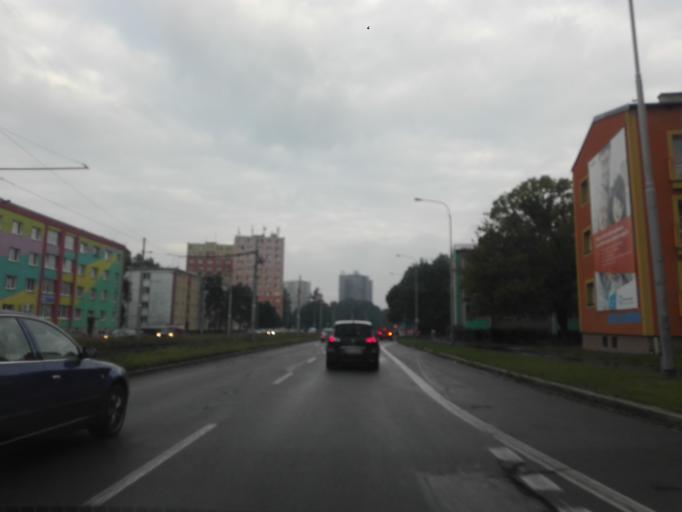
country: CZ
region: Moravskoslezsky
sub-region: Okres Ostrava-Mesto
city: Ostrava
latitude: 49.7915
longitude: 18.2523
